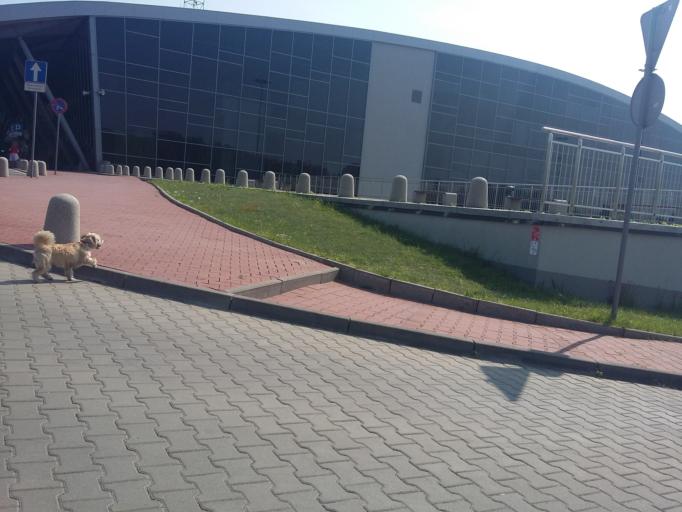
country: PL
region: Lodz Voivodeship
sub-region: Powiat pabianicki
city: Ksawerow
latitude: 51.7273
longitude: 19.3996
